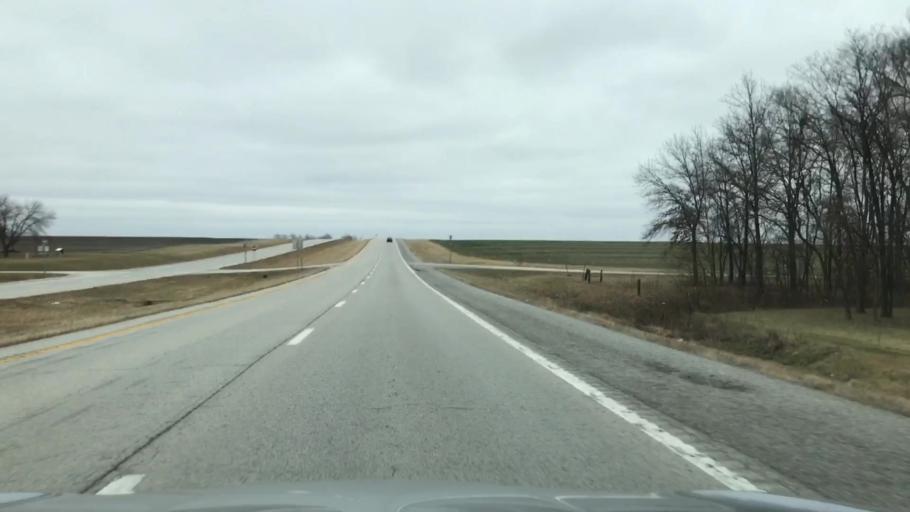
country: US
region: Missouri
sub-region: Livingston County
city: Chillicothe
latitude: 39.7761
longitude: -93.4833
